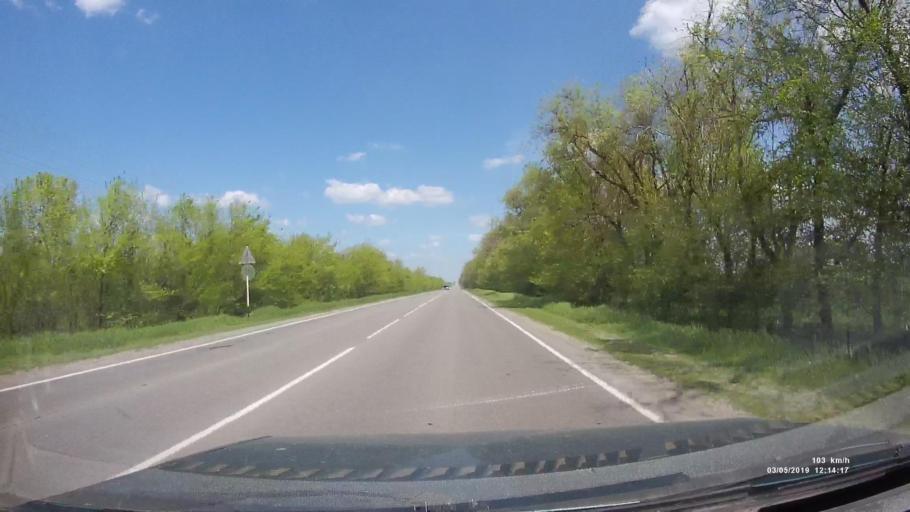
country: RU
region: Rostov
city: Melikhovskaya
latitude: 47.3419
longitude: 40.5618
